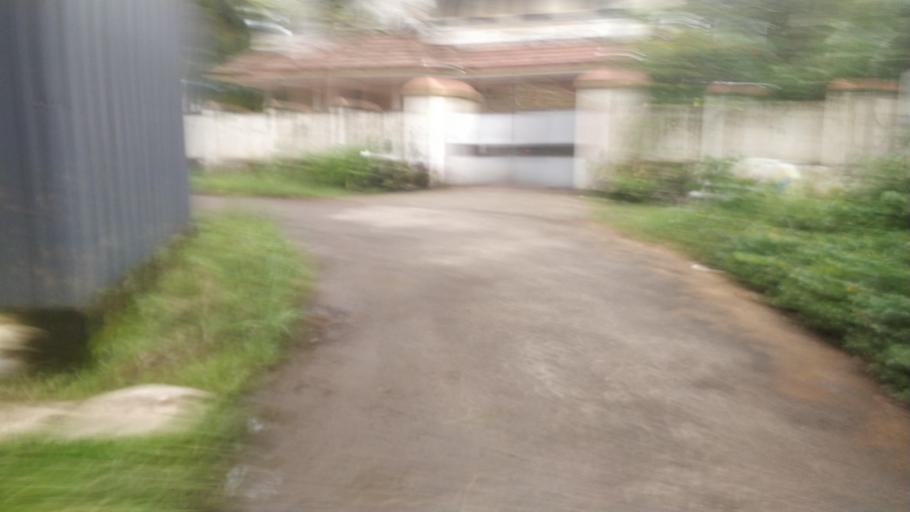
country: IN
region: Kerala
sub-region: Alappuzha
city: Vayalar
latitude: 9.7084
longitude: 76.3511
